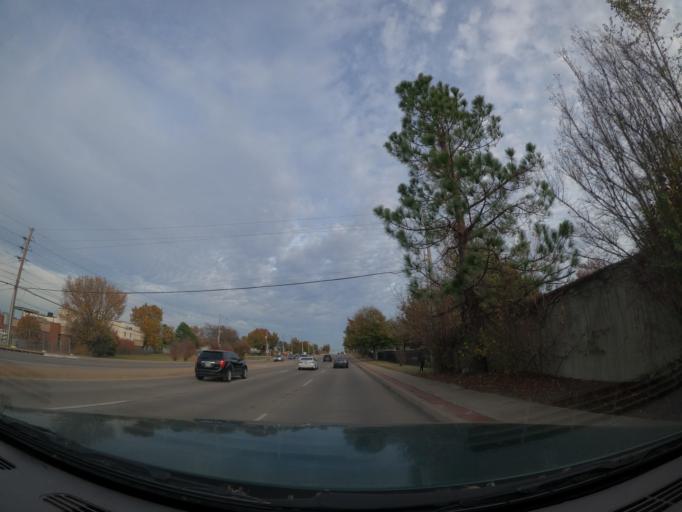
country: US
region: Oklahoma
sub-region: Tulsa County
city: Jenks
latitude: 36.0607
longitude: -95.9178
